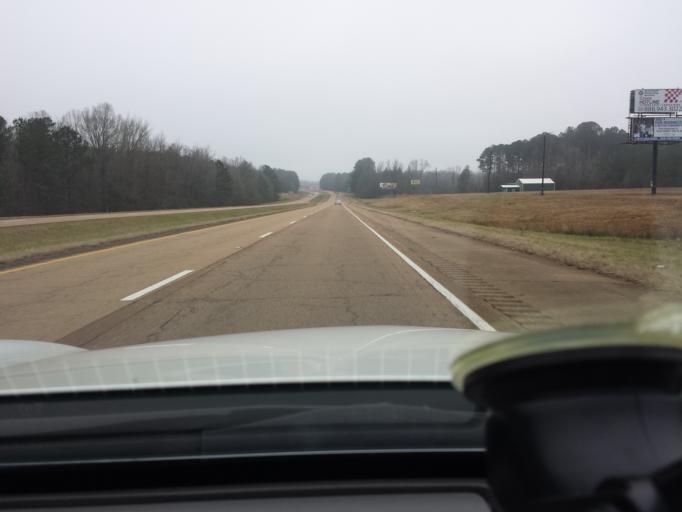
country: US
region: Mississippi
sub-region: Winston County
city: Louisville
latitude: 33.1449
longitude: -89.0869
